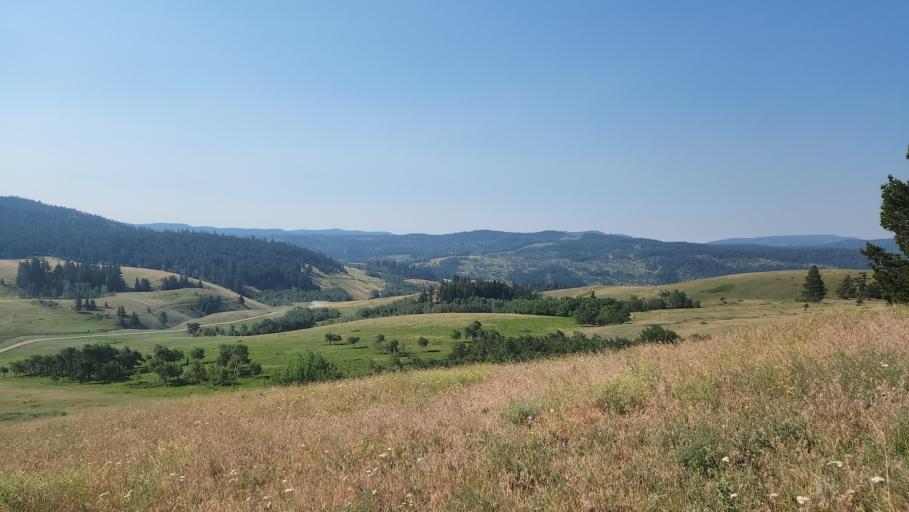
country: CA
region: British Columbia
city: Merritt
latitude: 50.0812
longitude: -120.6549
